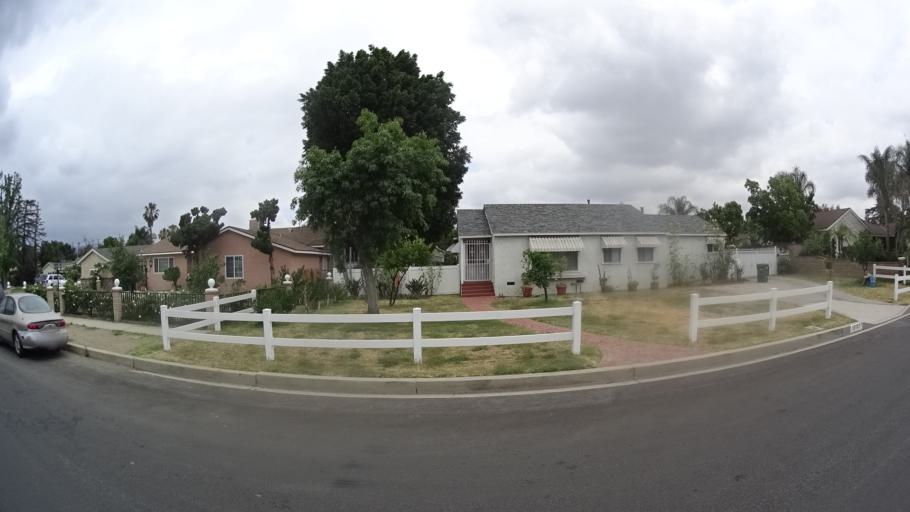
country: US
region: California
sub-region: Los Angeles County
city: San Fernando
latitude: 34.2633
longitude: -118.4630
